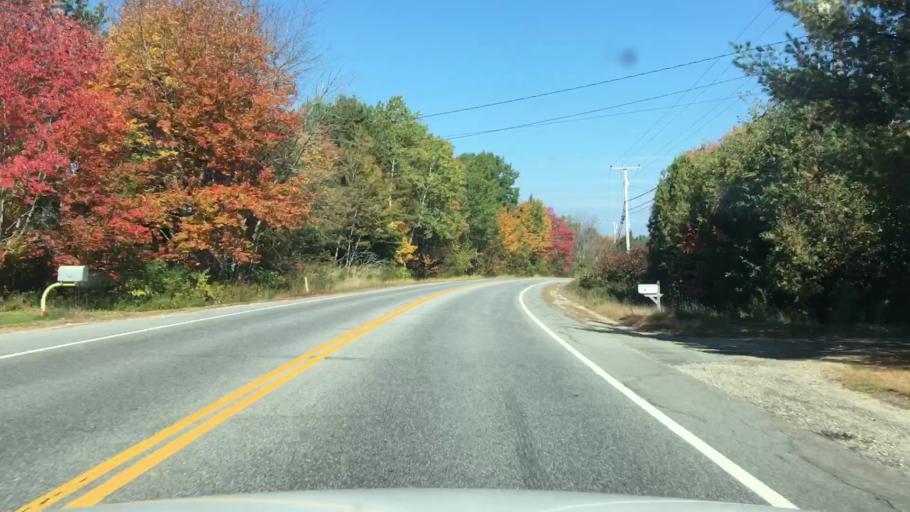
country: US
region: Maine
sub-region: Sagadahoc County
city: Topsham
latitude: 43.9788
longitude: -69.9609
